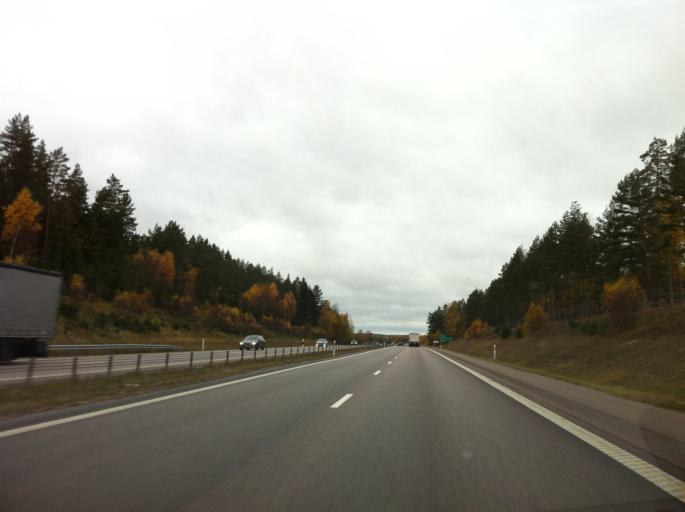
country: SE
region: OEstergoetland
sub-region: Mjolby Kommun
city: Mjolby
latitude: 58.3491
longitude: 15.1936
